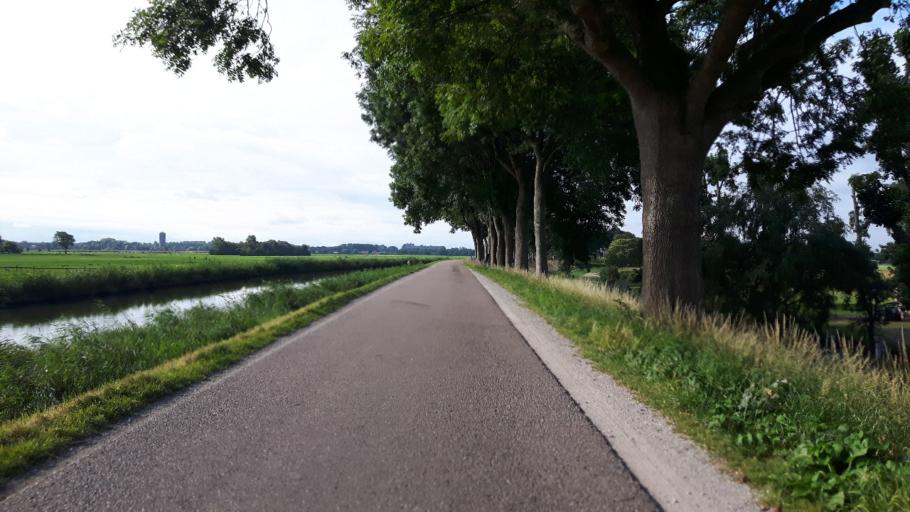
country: NL
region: North Holland
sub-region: Gemeente Purmerend
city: Purmerend
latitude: 52.5465
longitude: 4.9761
